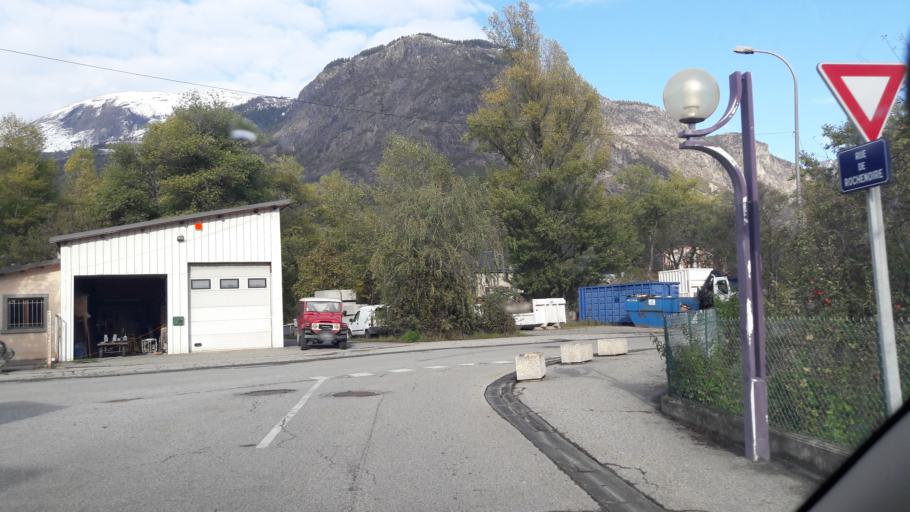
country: FR
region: Rhone-Alpes
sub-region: Departement de la Savoie
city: Saint-Jean-de-Maurienne
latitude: 45.2700
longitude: 6.3524
